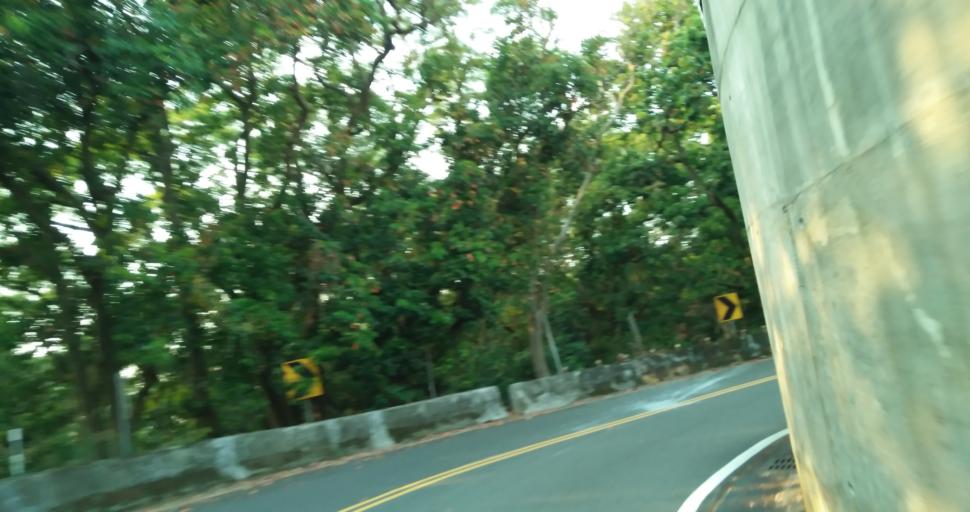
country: TW
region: Taiwan
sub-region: Hsinchu
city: Hsinchu
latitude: 24.7763
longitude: 120.9768
